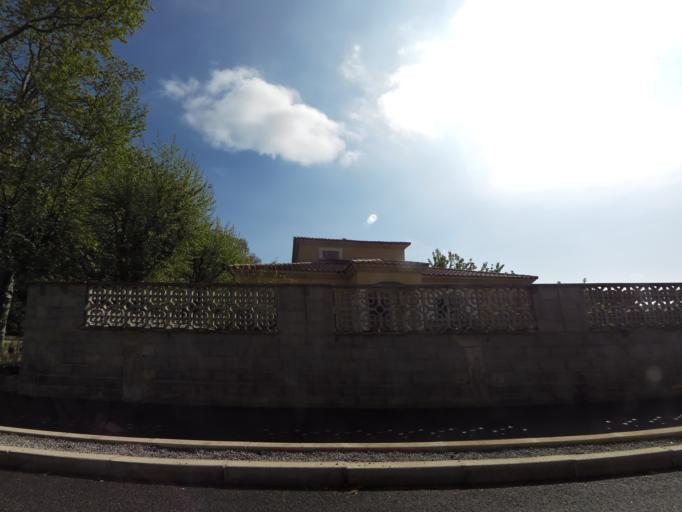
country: FR
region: Languedoc-Roussillon
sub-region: Departement du Gard
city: Aimargues
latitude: 43.6886
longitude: 4.2070
